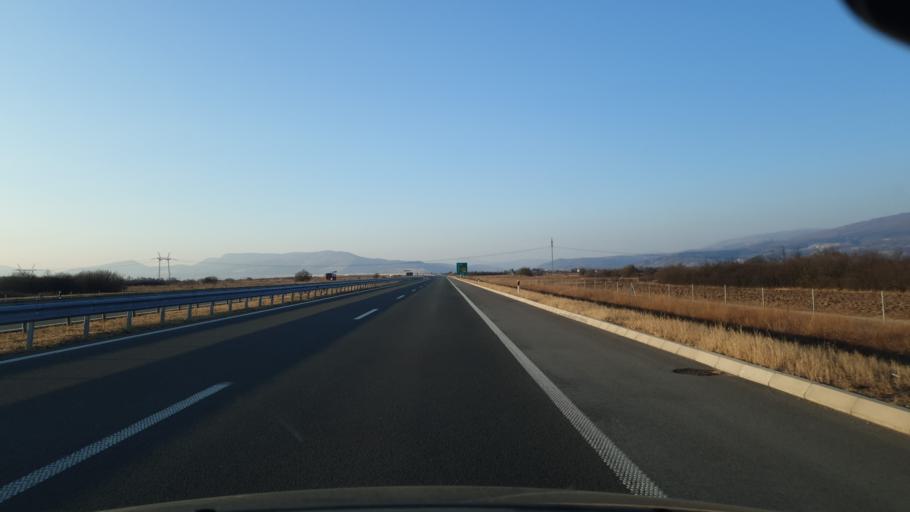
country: RS
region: Central Serbia
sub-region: Pirotski Okrug
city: Pirot
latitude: 43.1099
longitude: 22.6334
